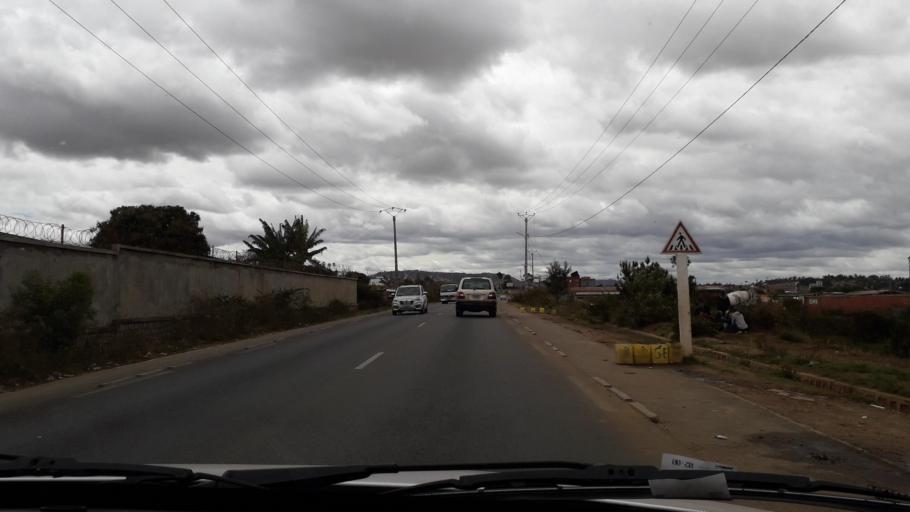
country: MG
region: Analamanga
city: Antananarivo
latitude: -18.8080
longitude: 47.4946
